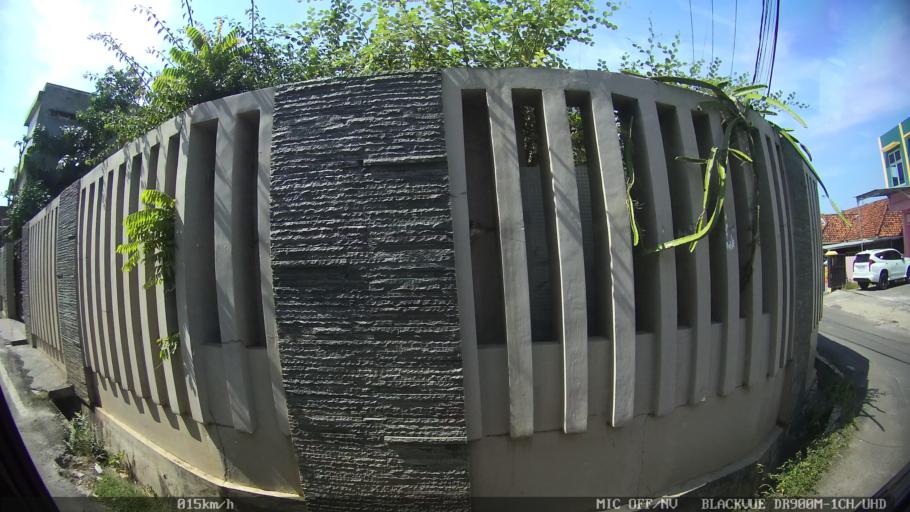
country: ID
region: Lampung
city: Kedaton
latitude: -5.3731
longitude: 105.2449
